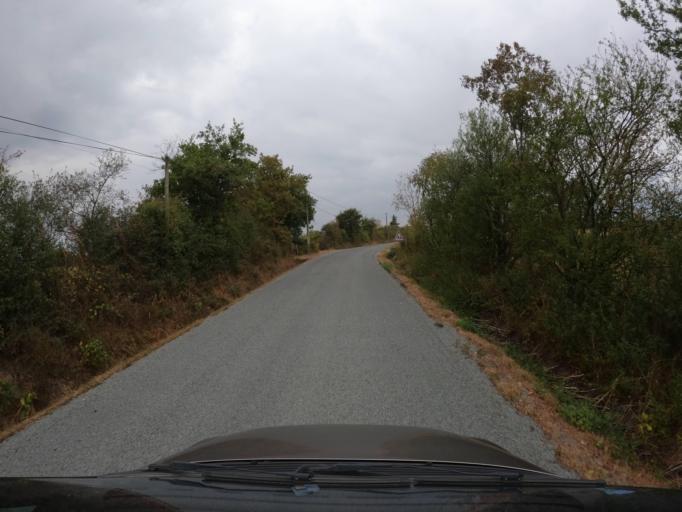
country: FR
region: Pays de la Loire
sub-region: Departement de la Vendee
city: Treize-Septiers
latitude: 46.9784
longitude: -1.2080
